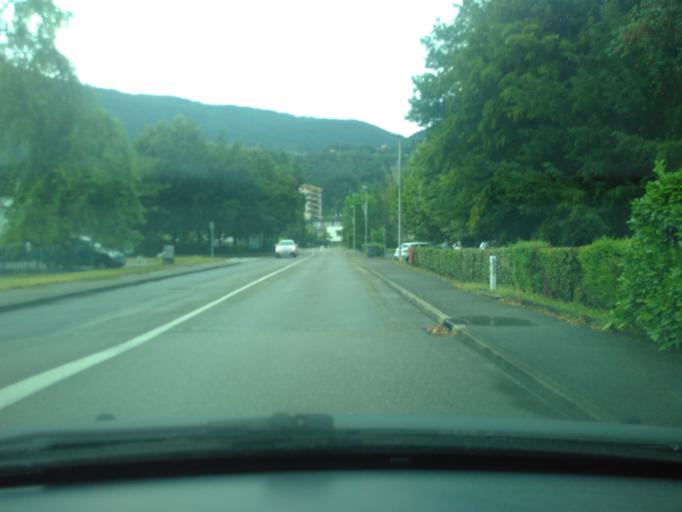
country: FR
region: Rhone-Alpes
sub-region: Departement de l'Isere
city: Corenc
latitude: 45.2079
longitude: 5.7681
